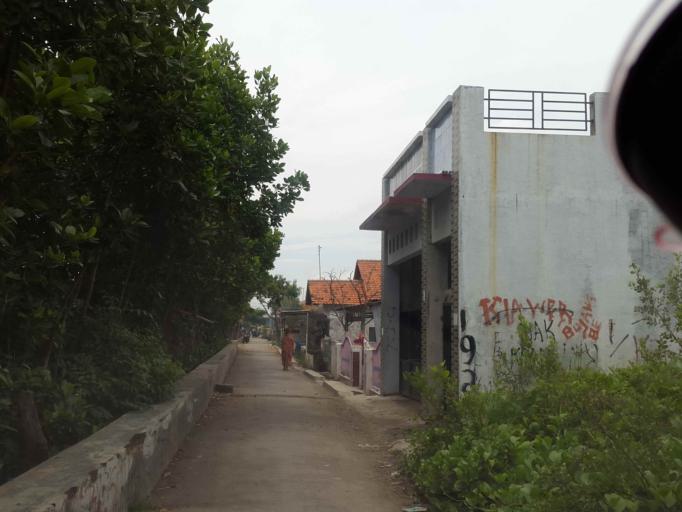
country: ID
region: Central Java
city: Tegal
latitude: -6.8476
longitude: 109.1146
